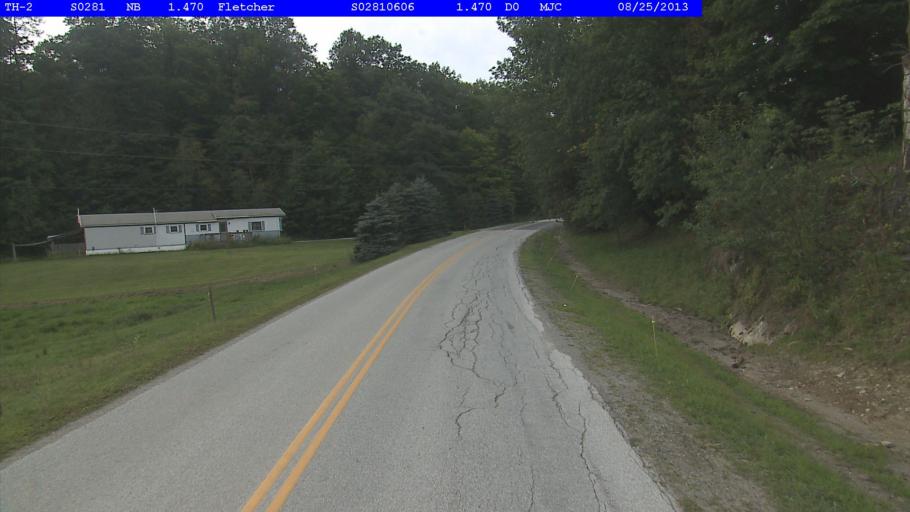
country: US
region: Vermont
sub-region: Chittenden County
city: Milton
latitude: 44.6965
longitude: -72.9349
